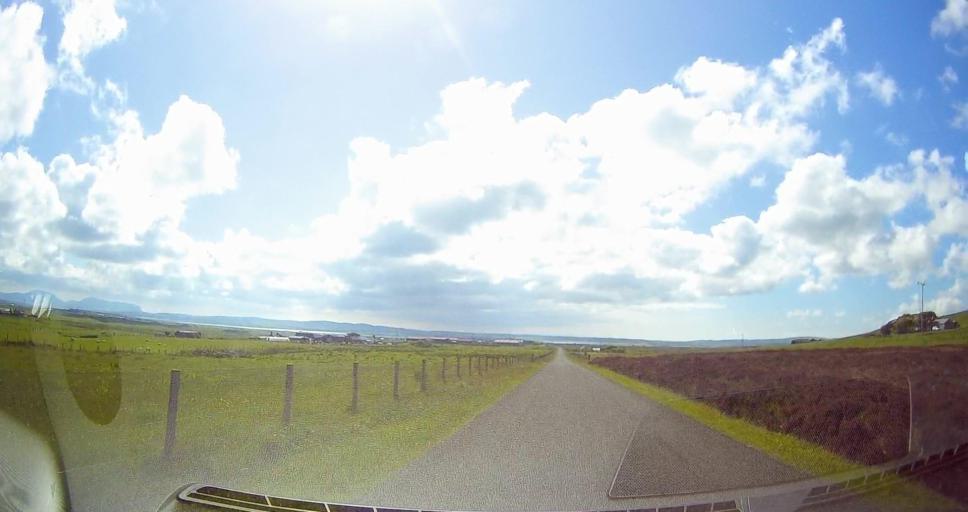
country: GB
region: Scotland
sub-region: Orkney Islands
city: Stromness
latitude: 59.0468
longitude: -3.1424
